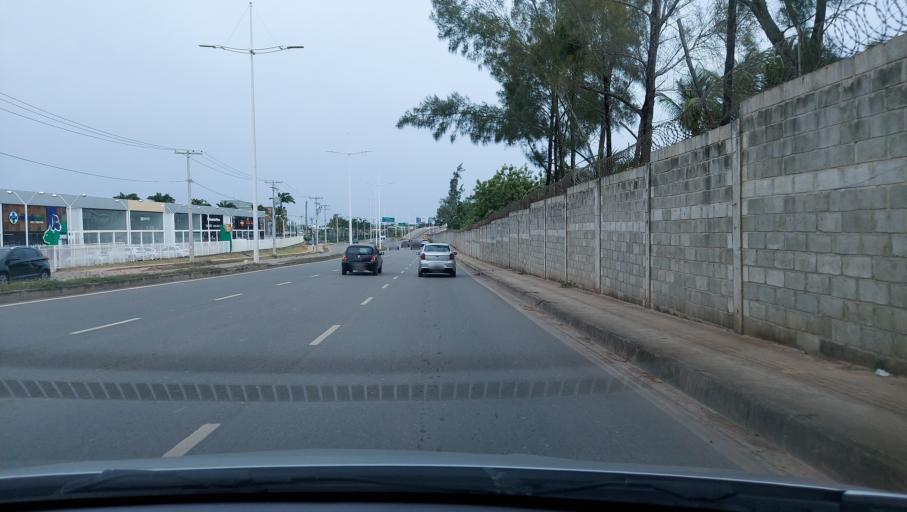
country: BR
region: Bahia
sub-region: Lauro De Freitas
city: Lauro de Freitas
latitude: -12.9430
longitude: -38.3858
